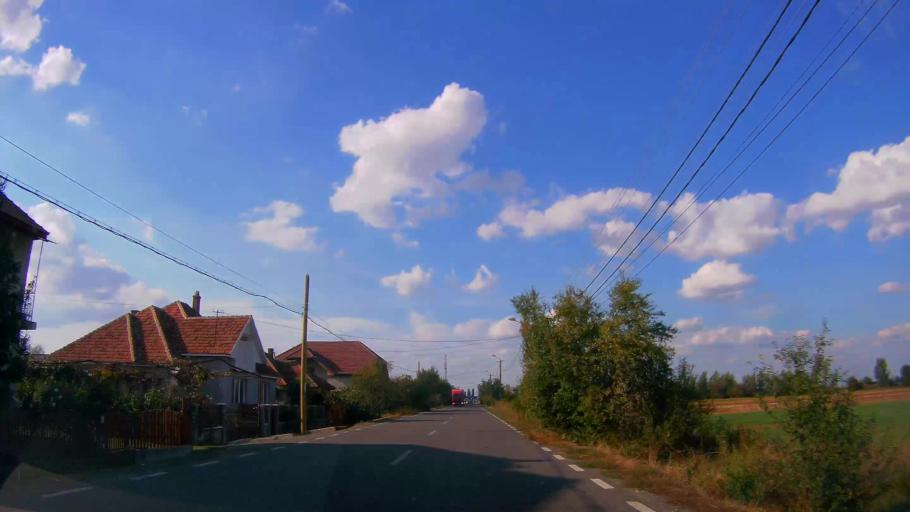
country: RO
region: Satu Mare
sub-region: Comuna Halmeu
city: Halmeu
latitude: 47.9879
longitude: 23.0056
